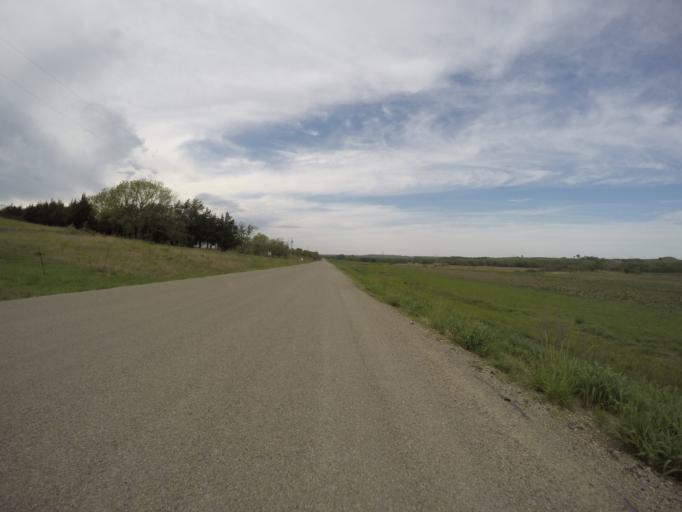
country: US
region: Kansas
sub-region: Riley County
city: Ogden
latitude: 39.0159
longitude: -96.6058
